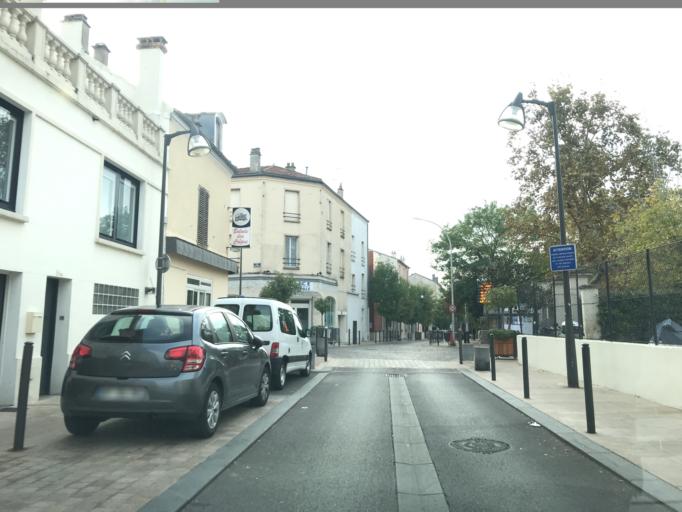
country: FR
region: Ile-de-France
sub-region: Departement du Val-de-Marne
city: Le Perreux-sur-Marne
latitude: 48.8409
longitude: 2.5050
